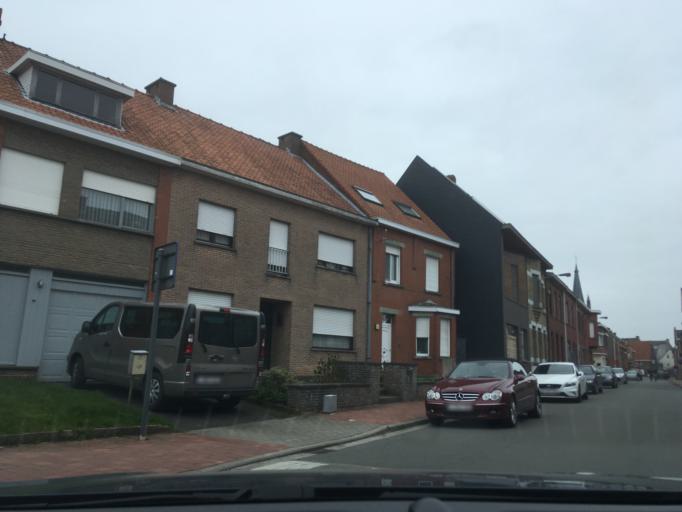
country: BE
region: Flanders
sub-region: Provincie West-Vlaanderen
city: Lichtervelde
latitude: 51.0295
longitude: 3.1382
